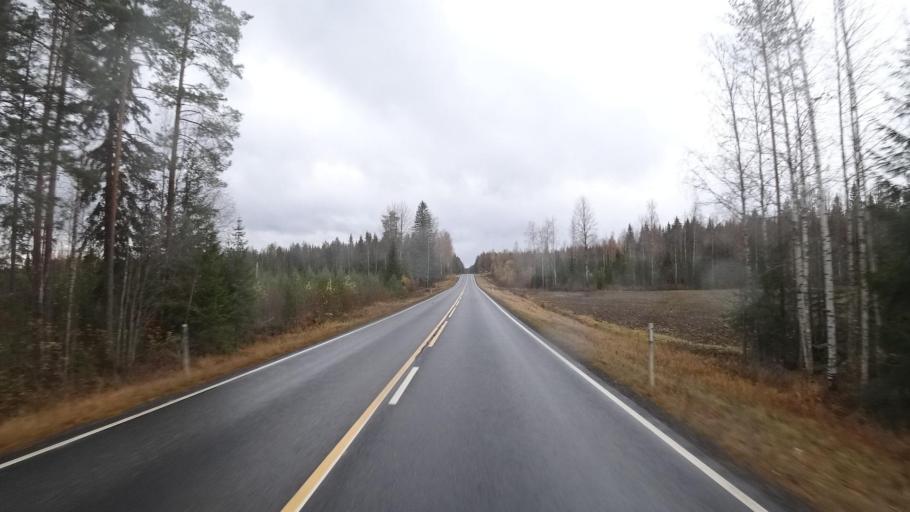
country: FI
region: Southern Savonia
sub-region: Mikkeli
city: Kangasniemi
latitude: 62.1661
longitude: 26.8447
